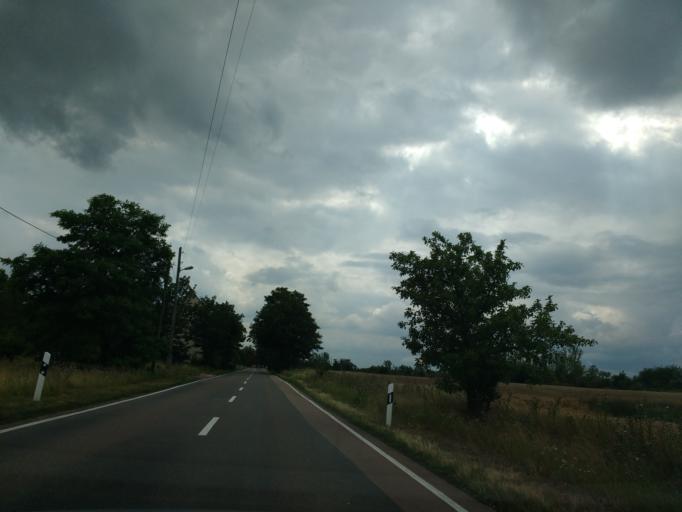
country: DE
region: Saxony-Anhalt
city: Dieskau
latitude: 51.4427
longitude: 12.0263
